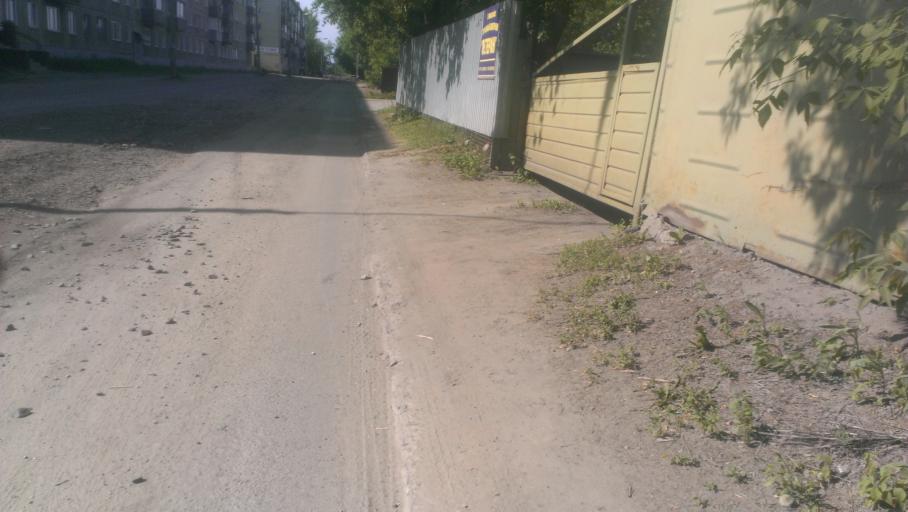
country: RU
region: Altai Krai
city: Novoaltaysk
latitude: 53.3951
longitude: 83.9367
